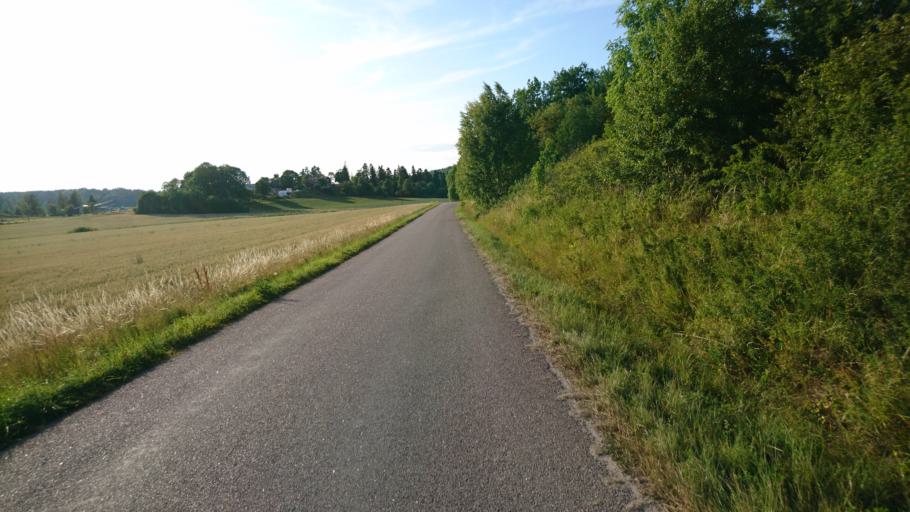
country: SE
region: Soedermanland
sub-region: Strangnas Kommun
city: Stallarholmen
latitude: 59.4008
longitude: 17.3002
